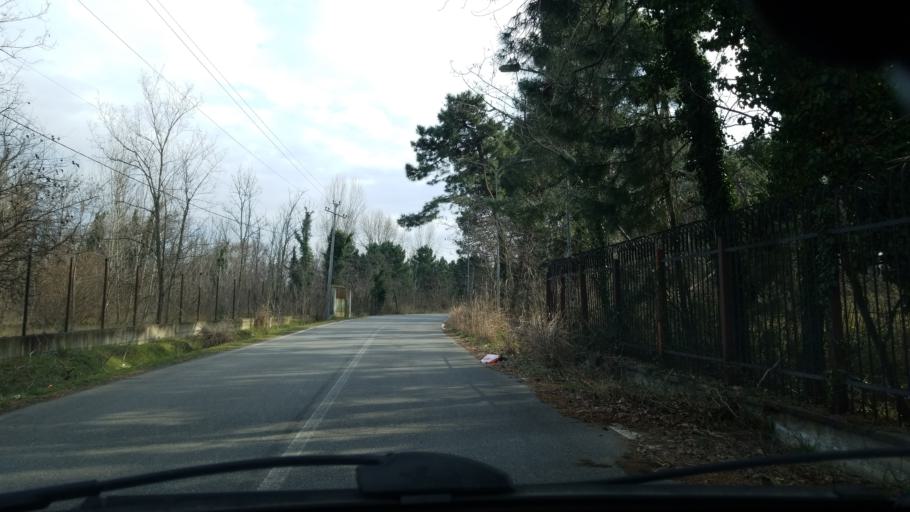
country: AL
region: Lezhe
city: Shengjin
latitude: 41.7818
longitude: 19.6038
